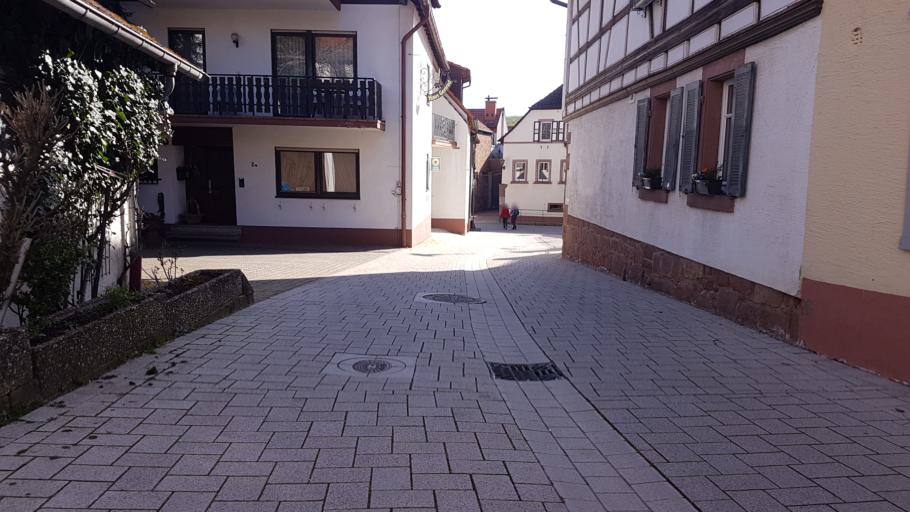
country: DE
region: Rheinland-Pfalz
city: Sankt Martin
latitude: 49.2999
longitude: 8.1051
